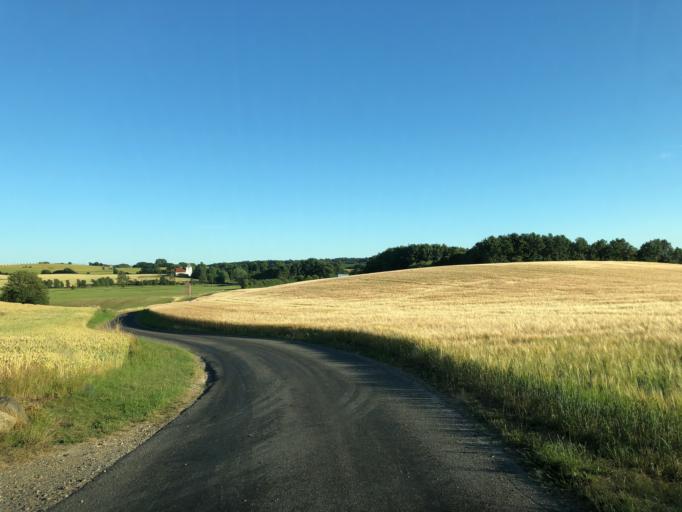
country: DK
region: Central Jutland
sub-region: Horsens Kommune
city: Horsens
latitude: 55.9373
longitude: 9.8659
